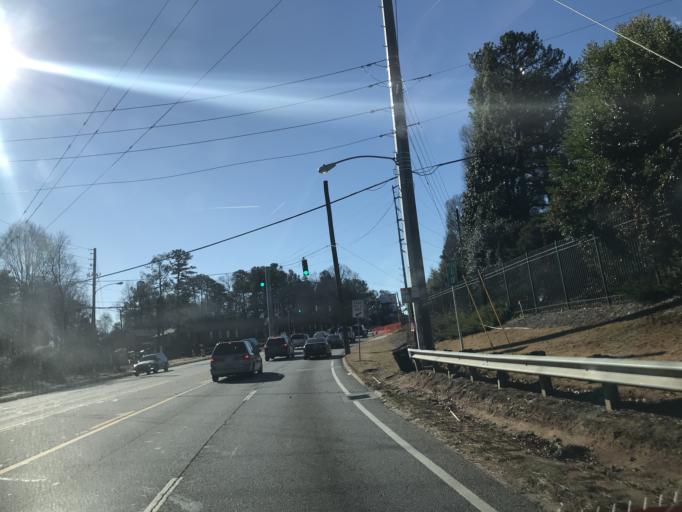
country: US
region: Georgia
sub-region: Fulton County
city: Sandy Springs
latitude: 33.9032
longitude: -84.3784
